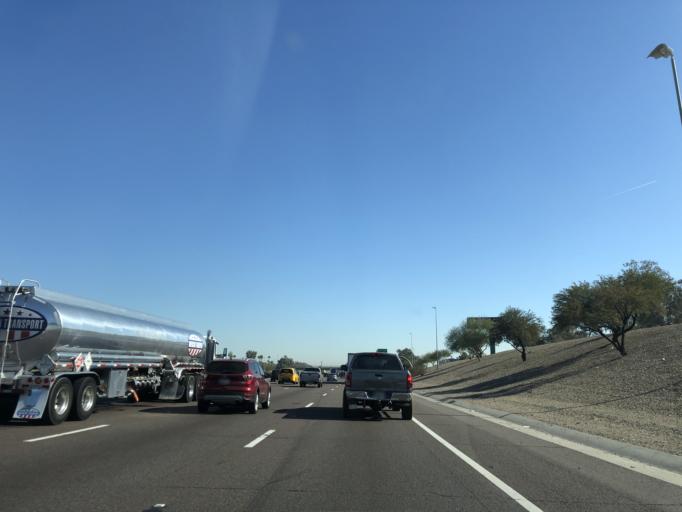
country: US
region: Arizona
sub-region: Maricopa County
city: Tolleson
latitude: 33.4620
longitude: -112.2450
